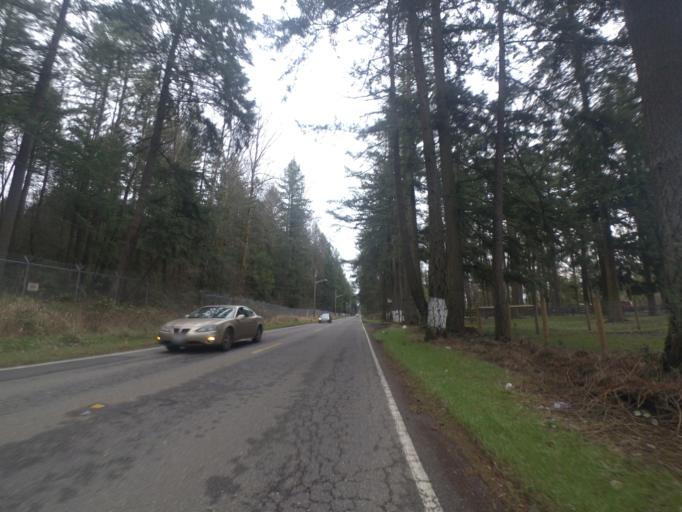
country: US
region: Washington
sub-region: Pierce County
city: McChord Air Force Base
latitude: 47.1212
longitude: -122.5200
